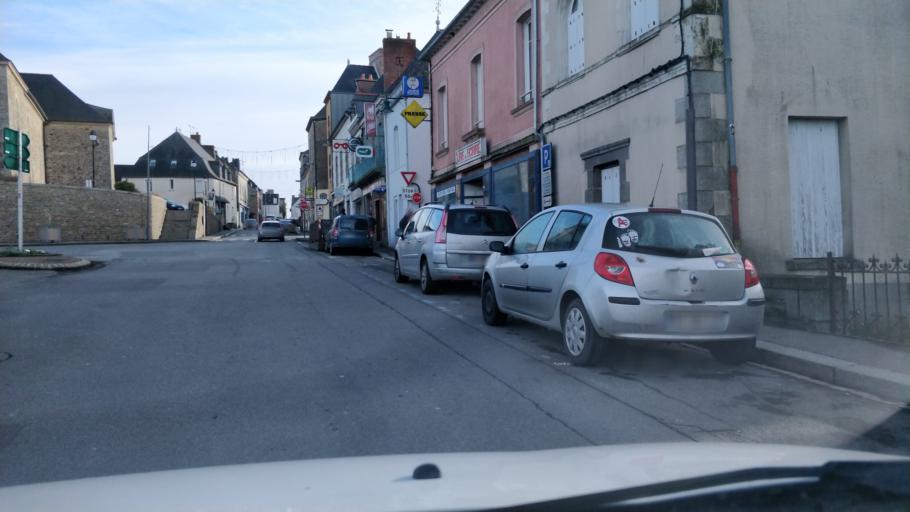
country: FR
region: Brittany
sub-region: Departement d'Ille-et-Vilaine
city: Argentre-du-Plessis
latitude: 48.0569
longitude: -1.1524
